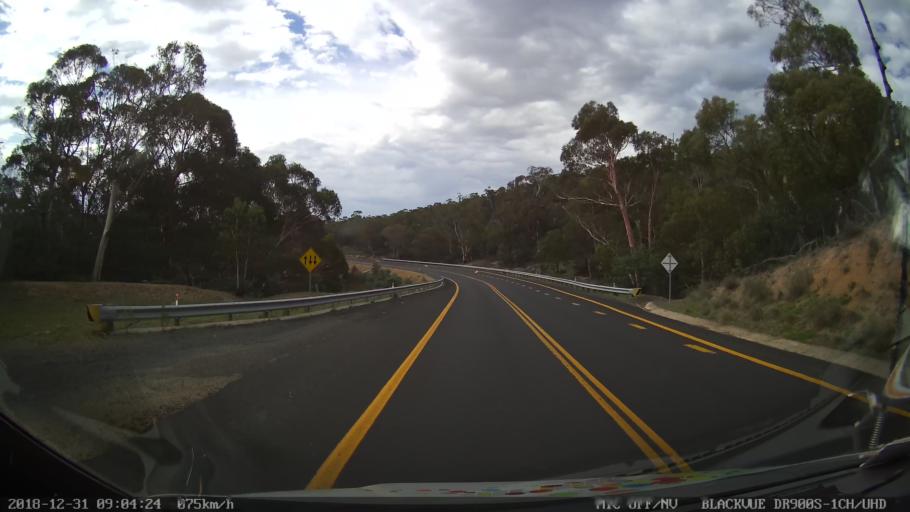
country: AU
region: New South Wales
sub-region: Snowy River
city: Jindabyne
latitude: -36.3539
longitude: 148.5866
